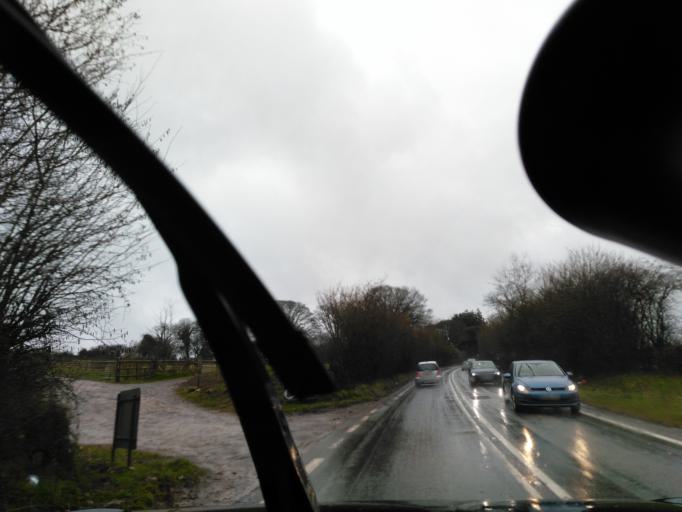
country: GB
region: England
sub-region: Somerset
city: Evercreech
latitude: 51.1955
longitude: -2.4660
